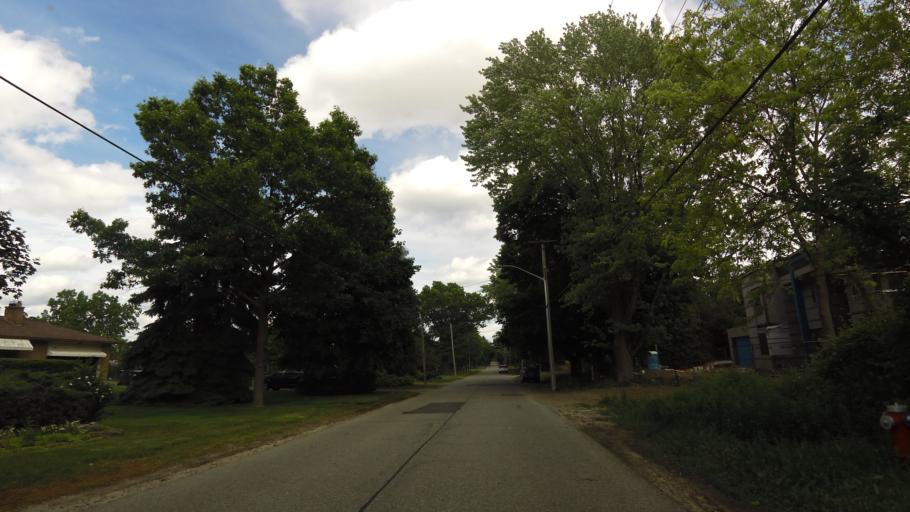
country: CA
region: Ontario
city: Mississauga
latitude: 43.5347
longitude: -79.6441
